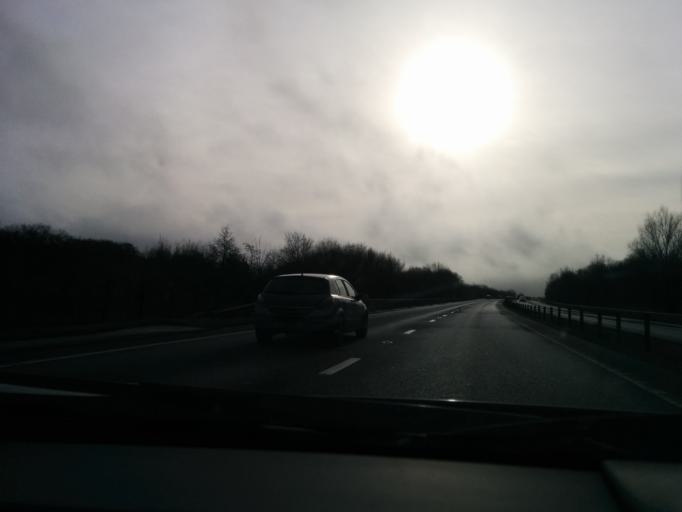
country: GB
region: England
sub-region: West Berkshire
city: Newbury
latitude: 51.4017
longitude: -1.3548
